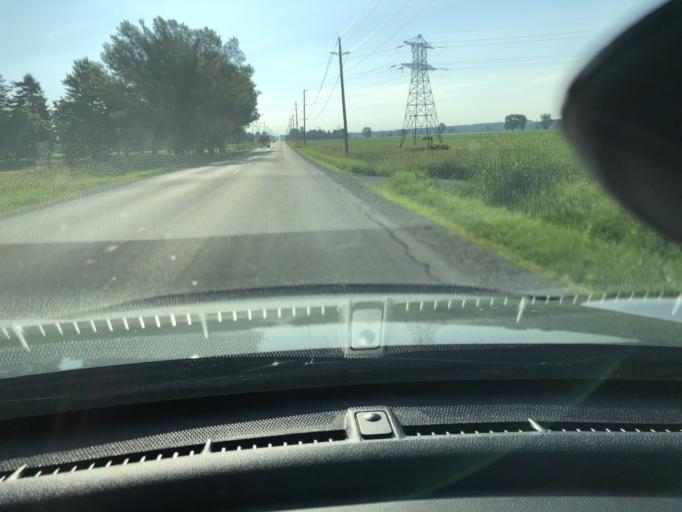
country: CA
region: Ontario
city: Stratford
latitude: 43.3892
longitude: -80.9460
